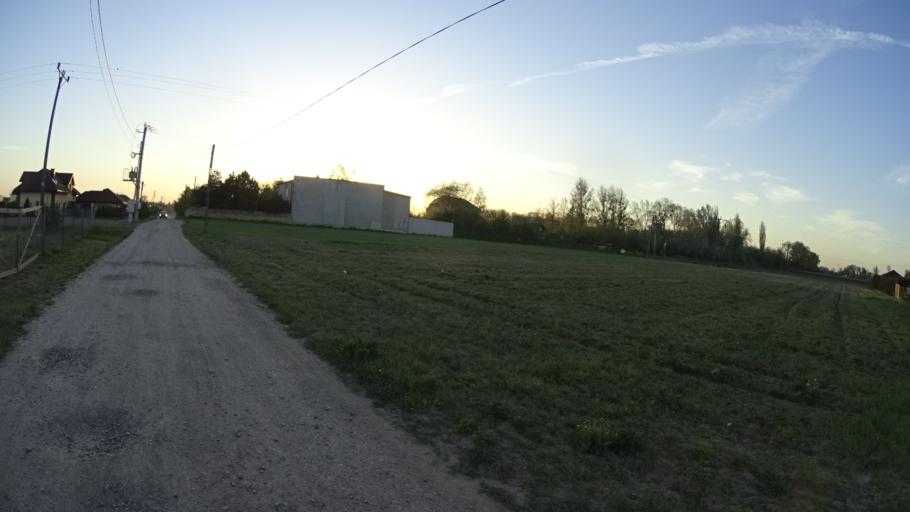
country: PL
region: Masovian Voivodeship
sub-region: Powiat warszawski zachodni
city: Ozarow Mazowiecki
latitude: 52.2293
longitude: 20.7872
